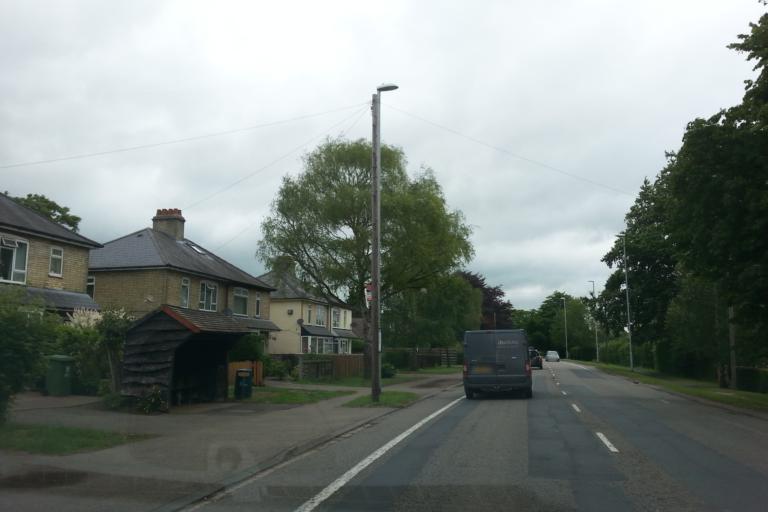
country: GB
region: England
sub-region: Cambridgeshire
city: Cambridge
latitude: 52.1579
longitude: 0.1277
